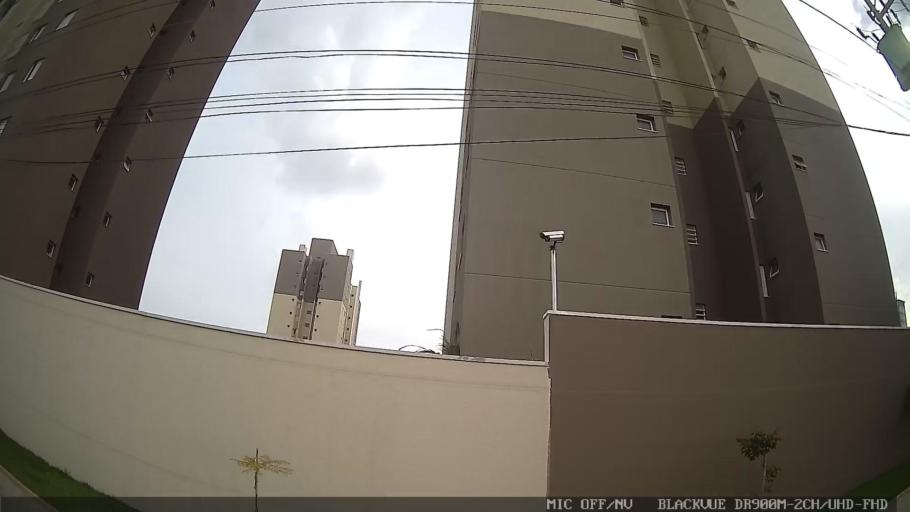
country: BR
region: Sao Paulo
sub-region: Indaiatuba
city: Indaiatuba
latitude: -23.0981
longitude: -47.1984
